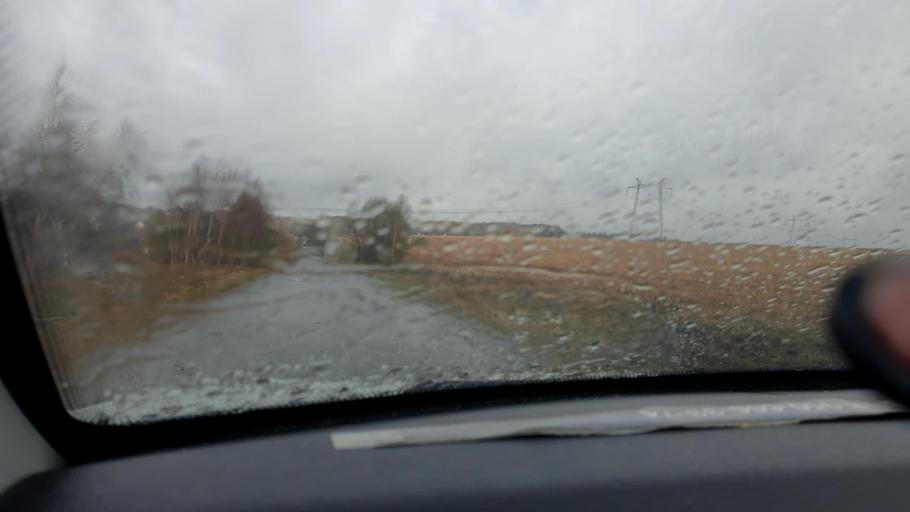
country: RU
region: Nizjnij Novgorod
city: Babino
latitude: 56.1684
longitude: 43.6784
